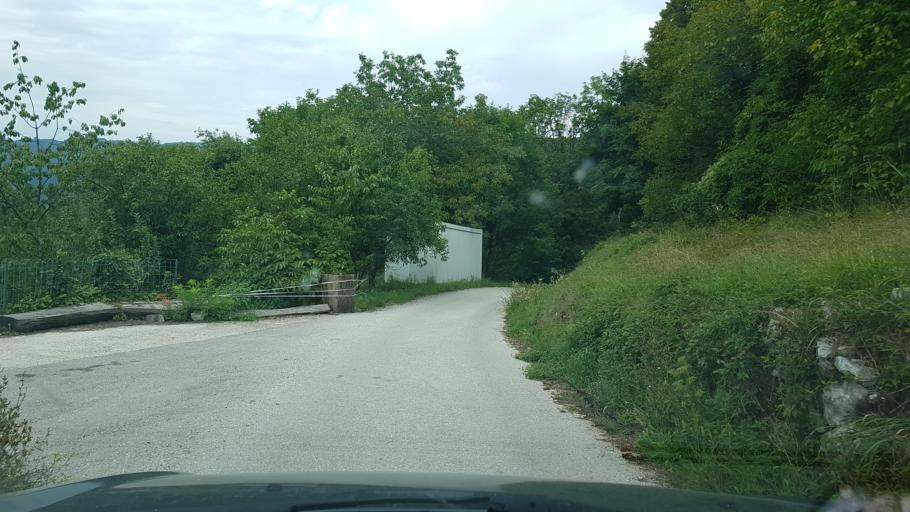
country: SI
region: Kanal
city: Deskle
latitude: 46.0212
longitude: 13.6172
